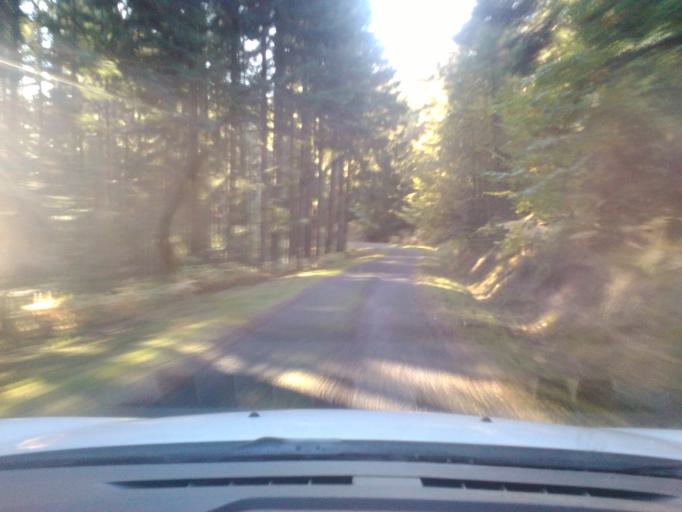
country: FR
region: Lorraine
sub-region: Departement des Vosges
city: Bruyeres
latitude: 48.2880
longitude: 6.7803
